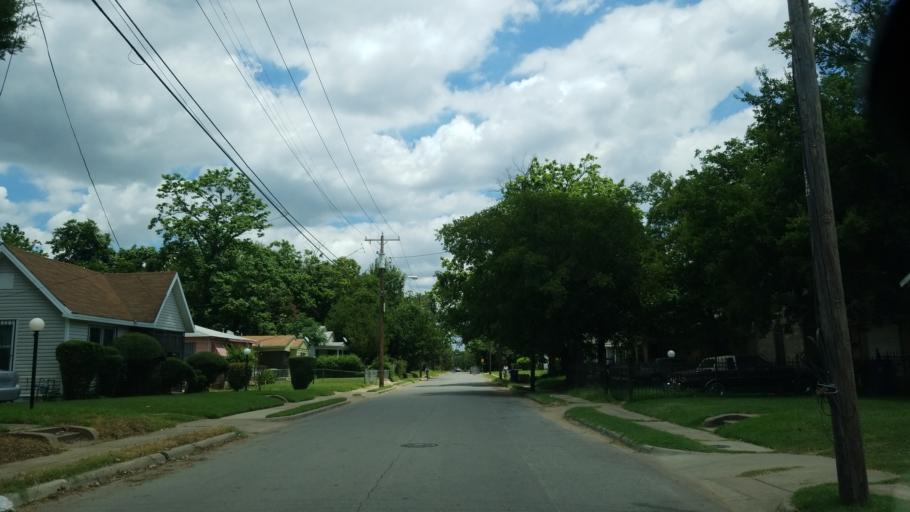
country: US
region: Texas
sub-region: Dallas County
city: Dallas
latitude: 32.7507
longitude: -96.7521
